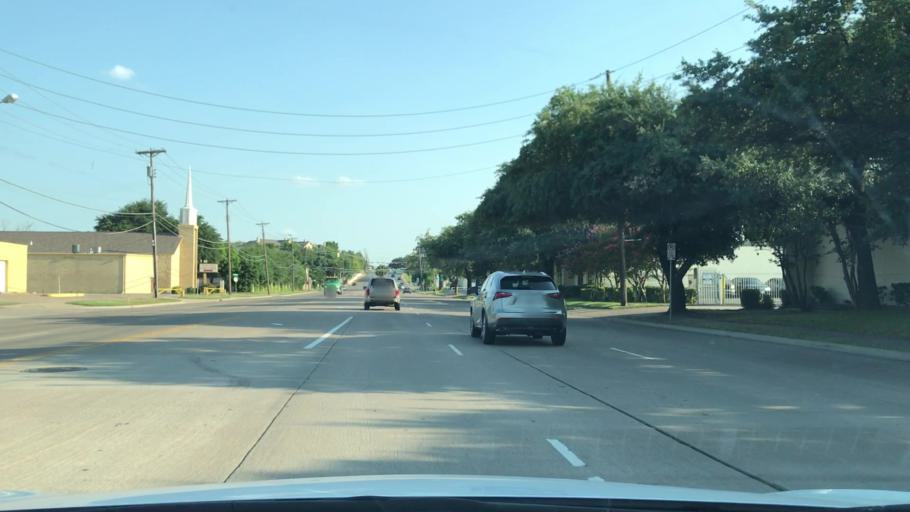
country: US
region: Texas
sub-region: Dallas County
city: Dallas
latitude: 32.7674
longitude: -96.8229
